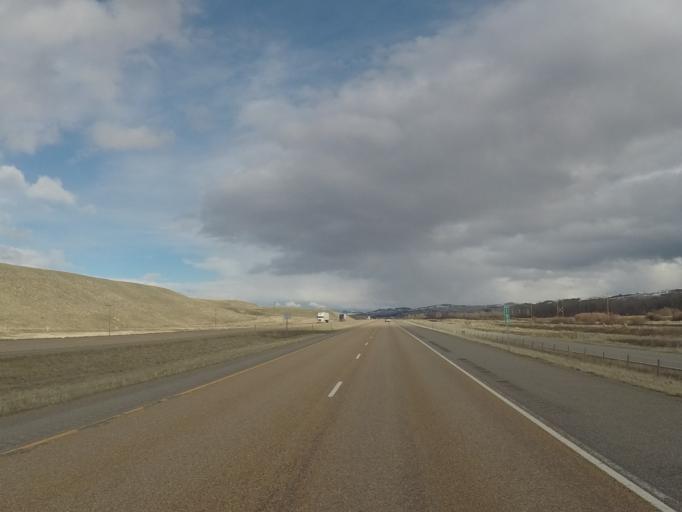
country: US
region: Montana
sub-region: Granite County
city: Philipsburg
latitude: 46.6290
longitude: -113.0815
